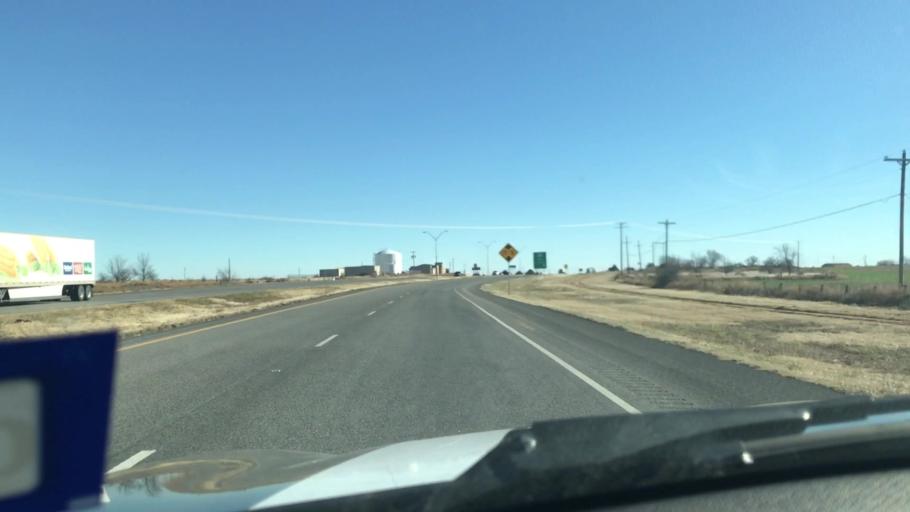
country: US
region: Texas
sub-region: Scurry County
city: Snyder
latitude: 32.7101
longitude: -100.8724
